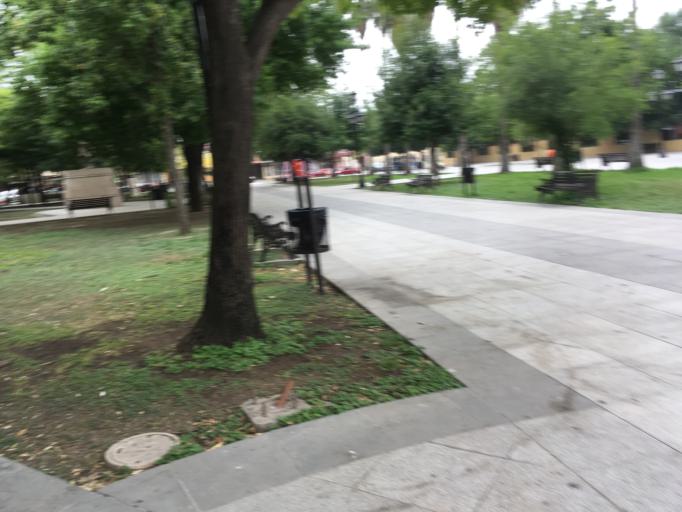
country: MX
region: Nuevo Leon
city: Guadalupe
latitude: 25.6768
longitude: -100.2588
